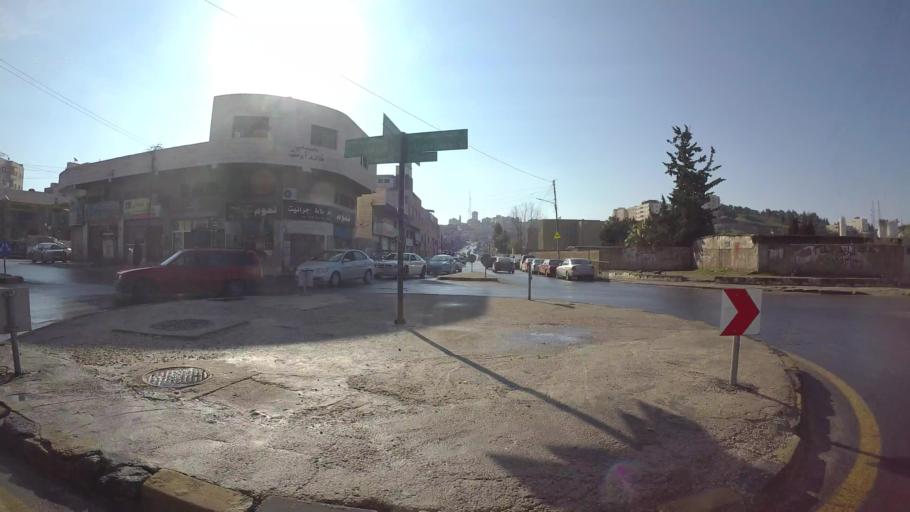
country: JO
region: Amman
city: Al Jubayhah
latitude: 32.0167
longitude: 35.8469
